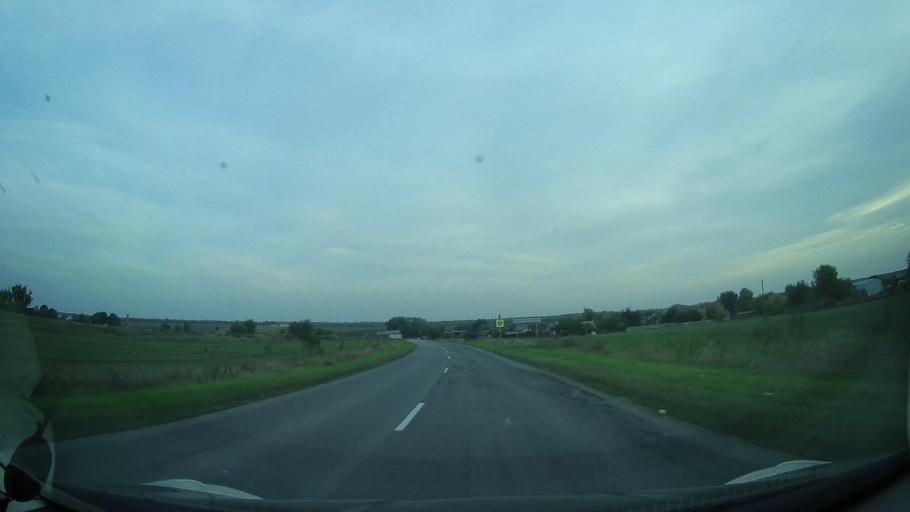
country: RU
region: Rostov
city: Kirovskaya
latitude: 47.0377
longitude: 39.9786
